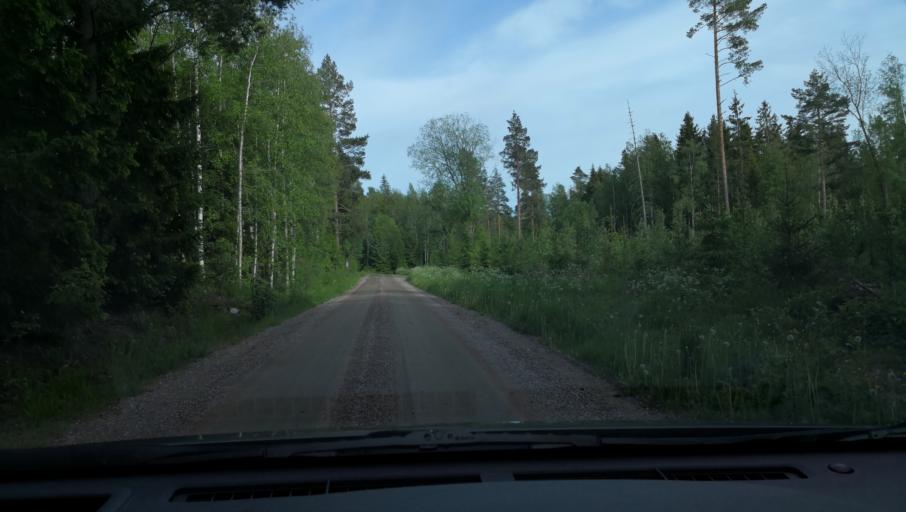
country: SE
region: Vaestmanland
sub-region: Kungsors Kommun
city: Kungsoer
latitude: 59.3580
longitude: 16.0579
